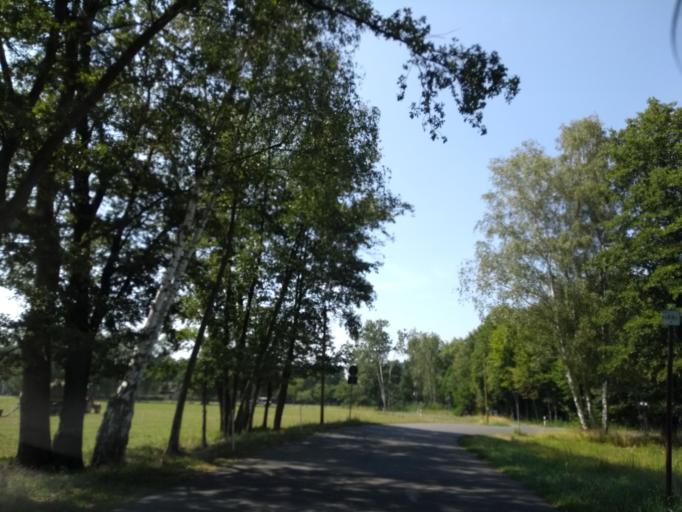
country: DE
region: Brandenburg
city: Burg
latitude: 51.8531
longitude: 14.1077
